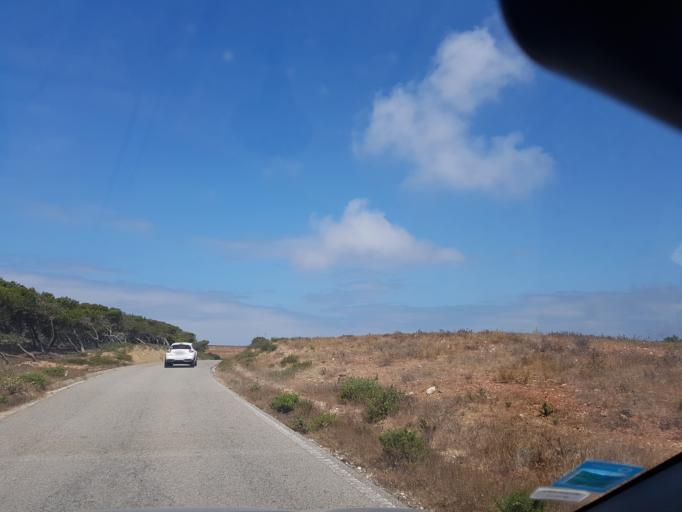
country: PT
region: Faro
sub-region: Vila do Bispo
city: Vila do Bispo
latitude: 37.0872
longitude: -8.9176
